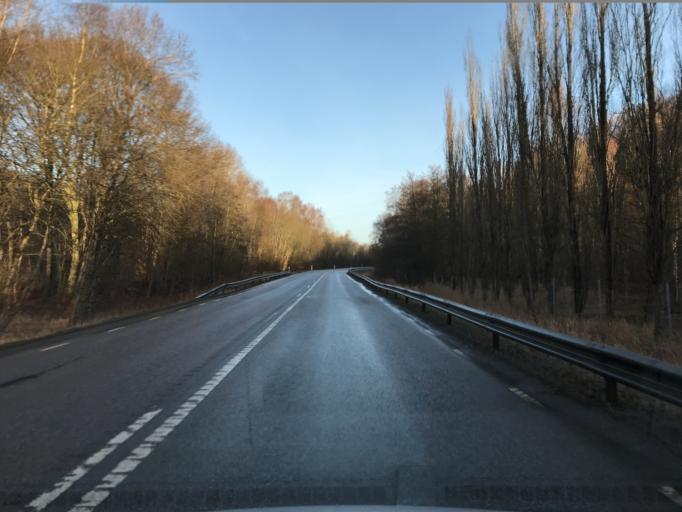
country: SE
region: Skane
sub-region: Hassleholms Kommun
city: Bjarnum
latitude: 56.2721
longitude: 13.7162
